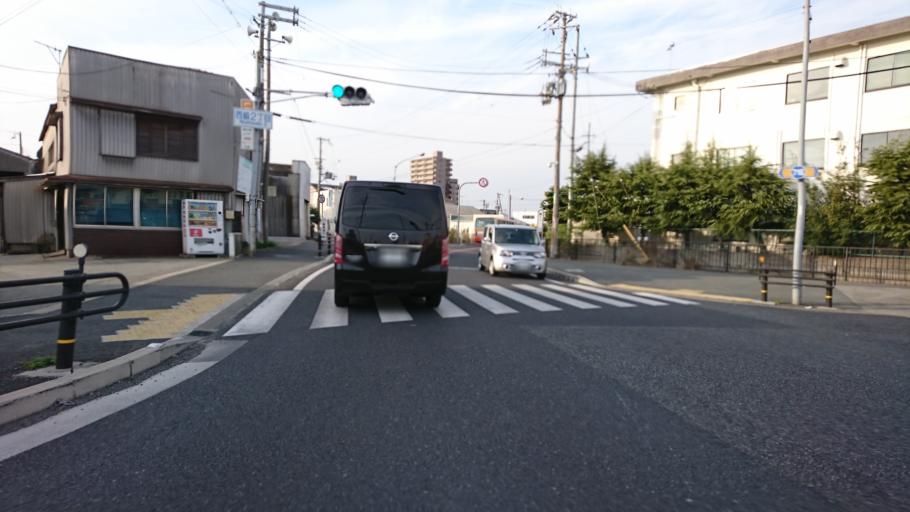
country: JP
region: Hyogo
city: Kakogawacho-honmachi
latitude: 34.7239
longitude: 134.8499
